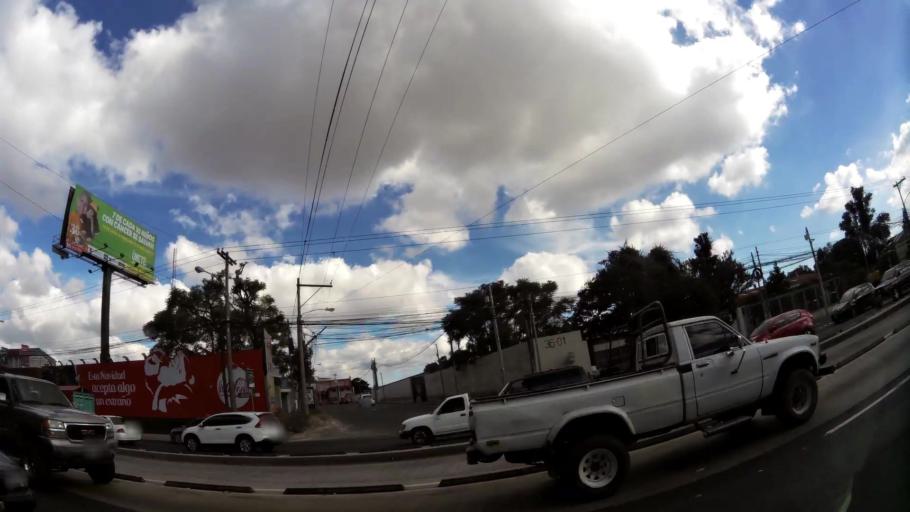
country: GT
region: Guatemala
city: Mixco
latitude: 14.5890
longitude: -90.5615
